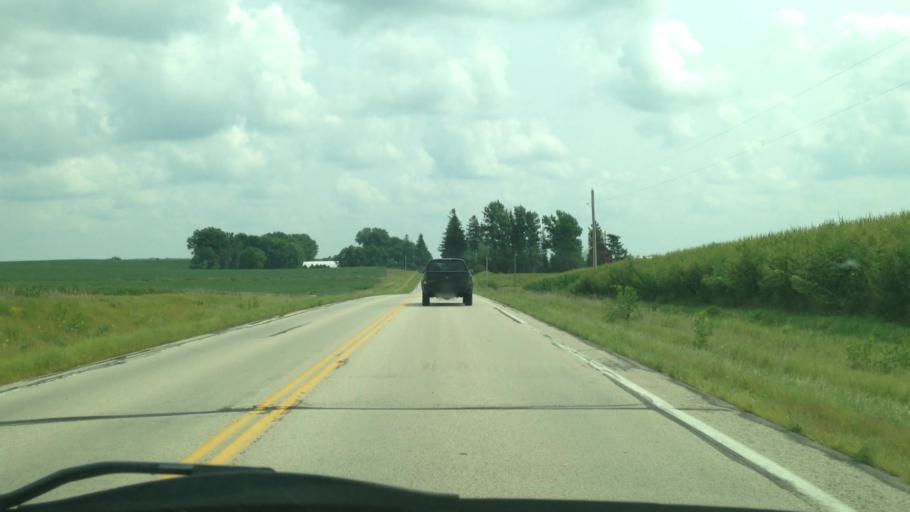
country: US
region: Minnesota
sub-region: Wabasha County
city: Elgin
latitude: 44.1367
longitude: -92.3377
